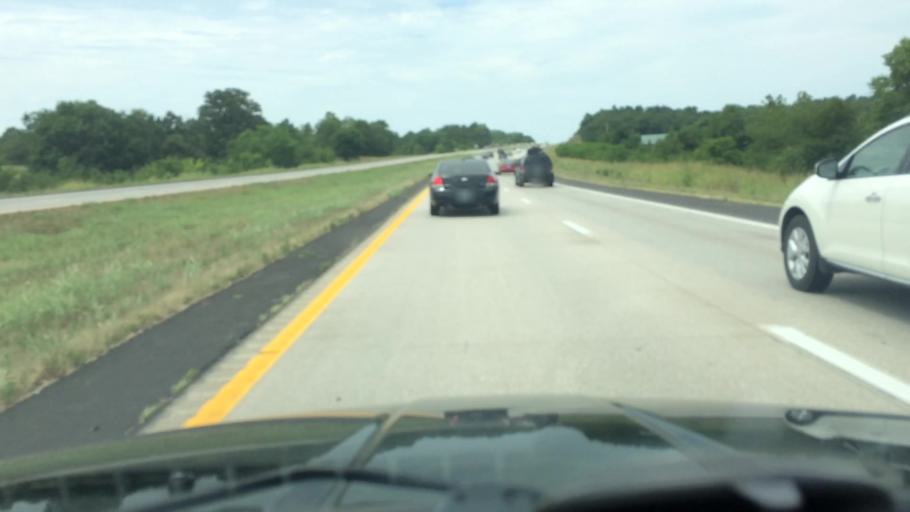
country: US
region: Missouri
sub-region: Greene County
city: Willard
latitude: 37.4332
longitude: -93.3554
